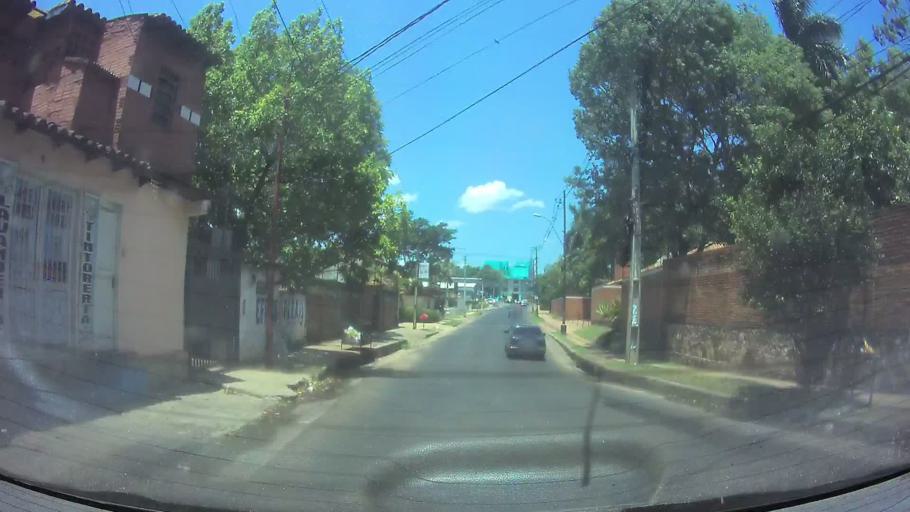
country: PY
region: Asuncion
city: Asuncion
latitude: -25.2941
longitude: -57.5941
